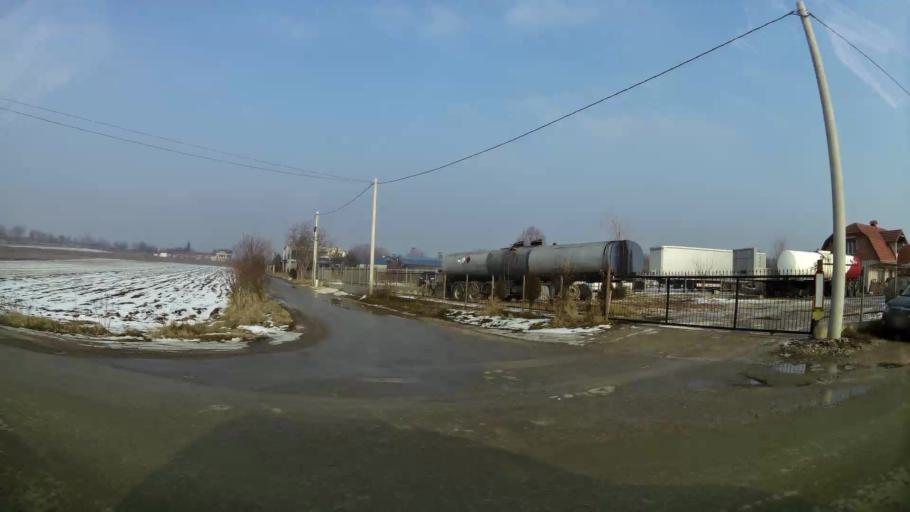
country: MK
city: Kadino
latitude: 41.9769
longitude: 21.6013
